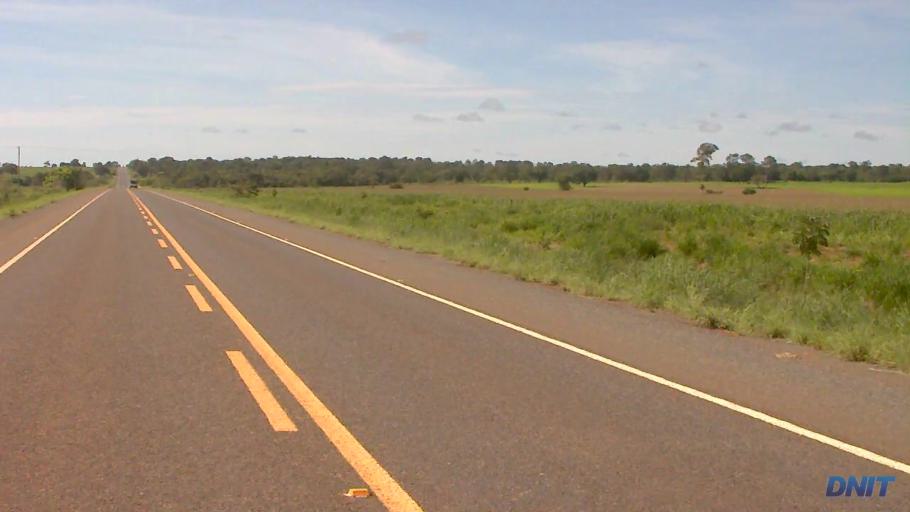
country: BR
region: Goias
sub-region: Sao Miguel Do Araguaia
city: Sao Miguel do Araguaia
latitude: -13.3885
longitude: -50.1386
